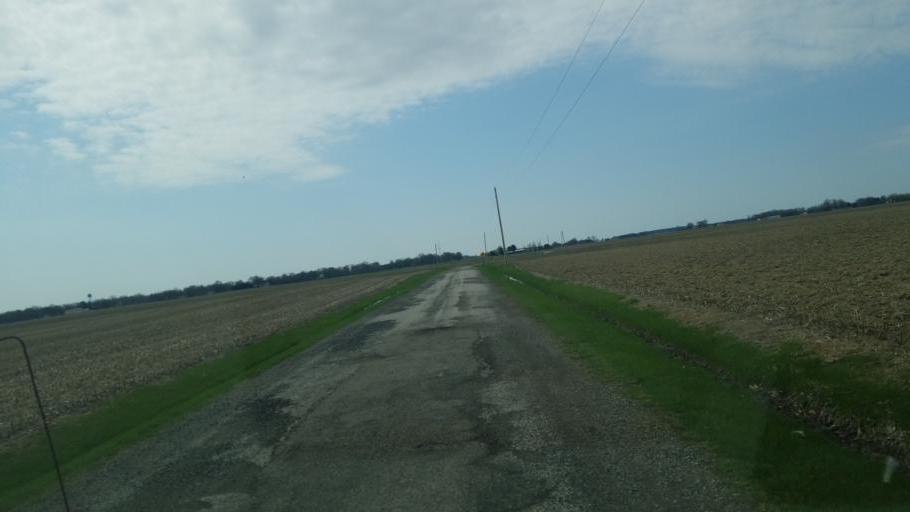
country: US
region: Ohio
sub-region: Delaware County
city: Ashley
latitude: 40.4269
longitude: -82.9624
